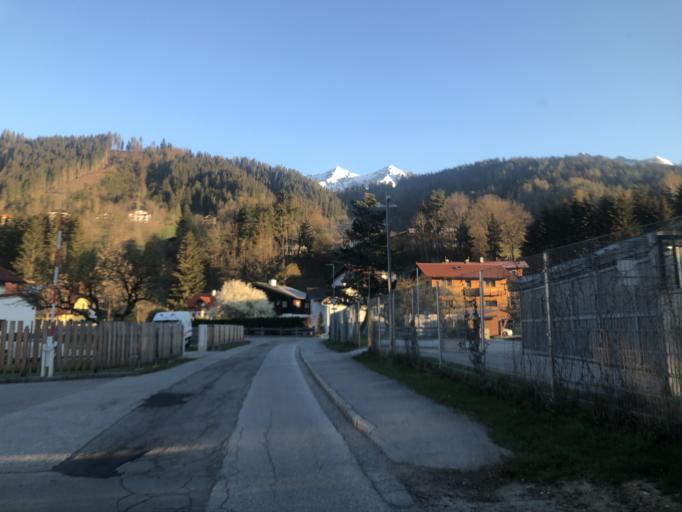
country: AT
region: Styria
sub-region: Politischer Bezirk Liezen
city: Schladming
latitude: 47.3996
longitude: 13.6997
